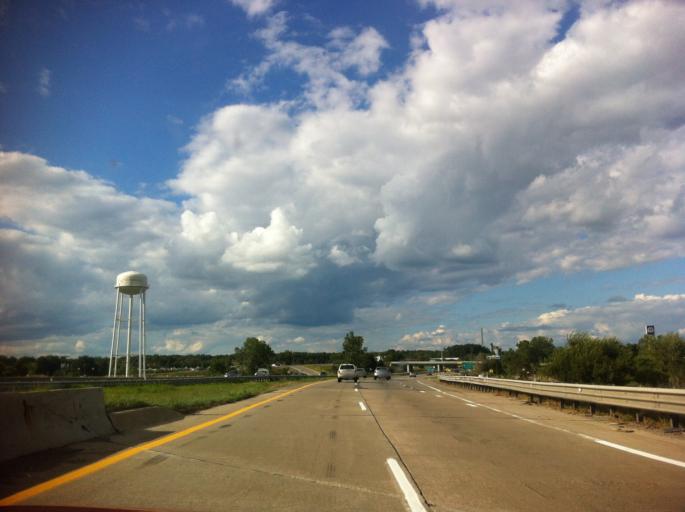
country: US
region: Michigan
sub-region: Livingston County
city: Whitmore Lake
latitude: 42.4250
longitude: -83.7683
